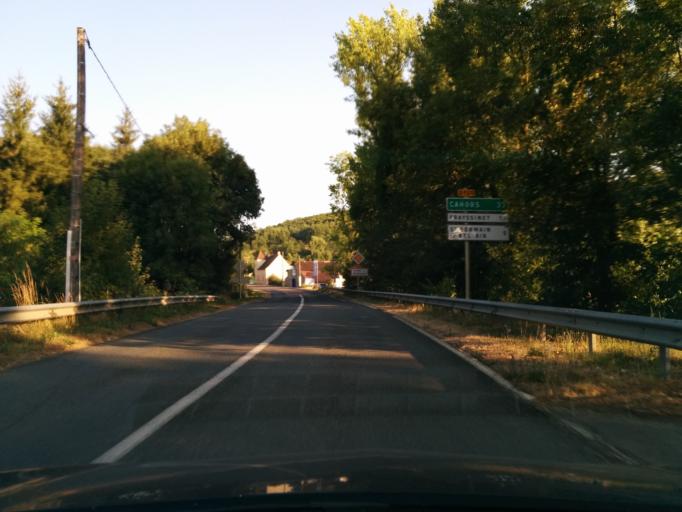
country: FR
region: Midi-Pyrenees
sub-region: Departement du Lot
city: Le Vigan
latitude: 44.6737
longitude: 1.4767
